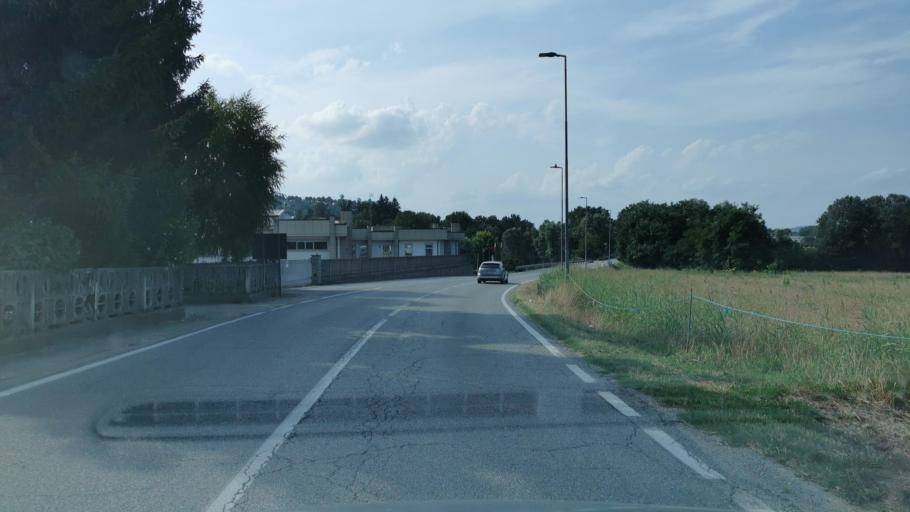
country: IT
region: Piedmont
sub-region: Provincia di Cuneo
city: Cherasco
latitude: 44.6464
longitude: 7.8761
